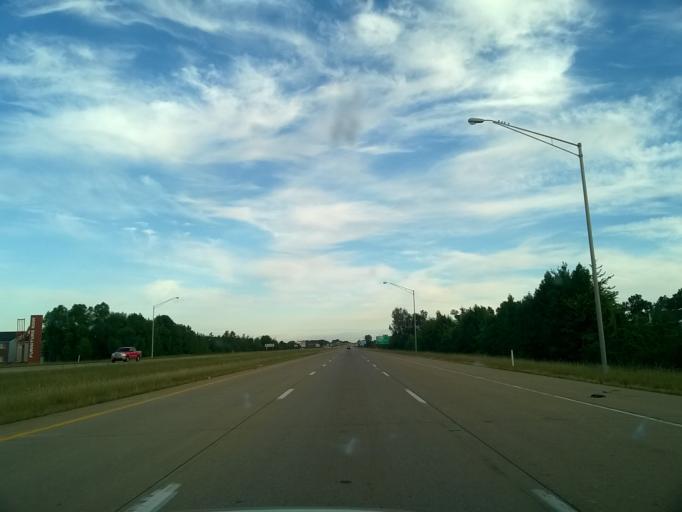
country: US
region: Indiana
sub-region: Warrick County
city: Newburgh
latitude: 37.9824
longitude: -87.4557
